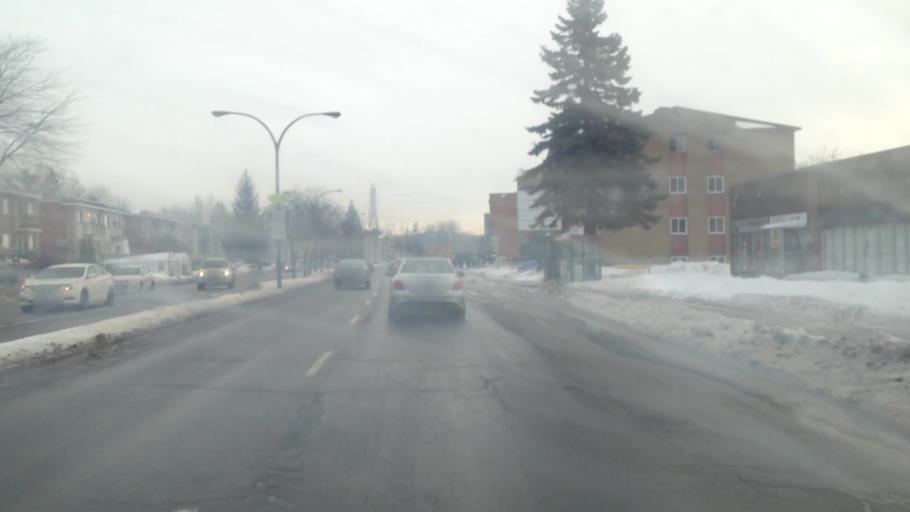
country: CA
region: Quebec
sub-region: Monteregie
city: Brossard
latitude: 45.4653
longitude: -73.4550
